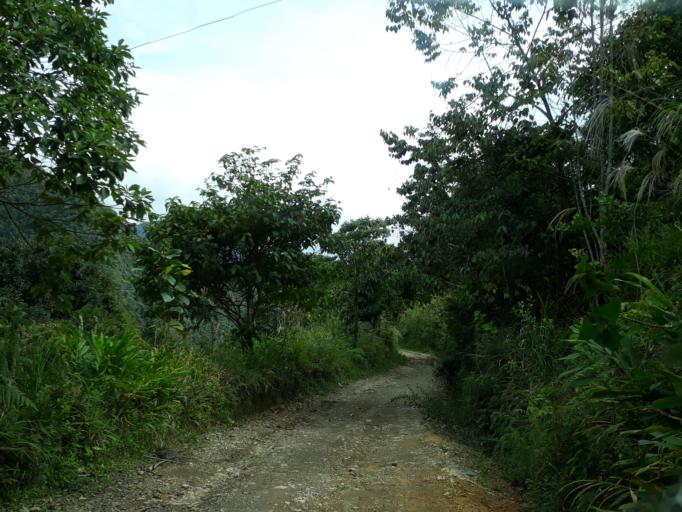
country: CO
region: Boyaca
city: Quipama
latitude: 5.3927
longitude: -74.1169
